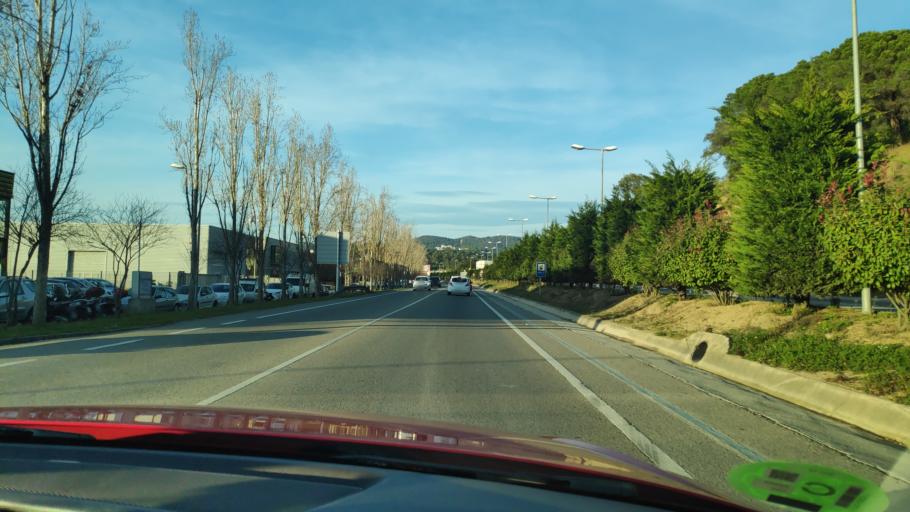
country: ES
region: Catalonia
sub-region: Provincia de Girona
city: Lloret de Mar
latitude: 41.7113
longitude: 2.8319
